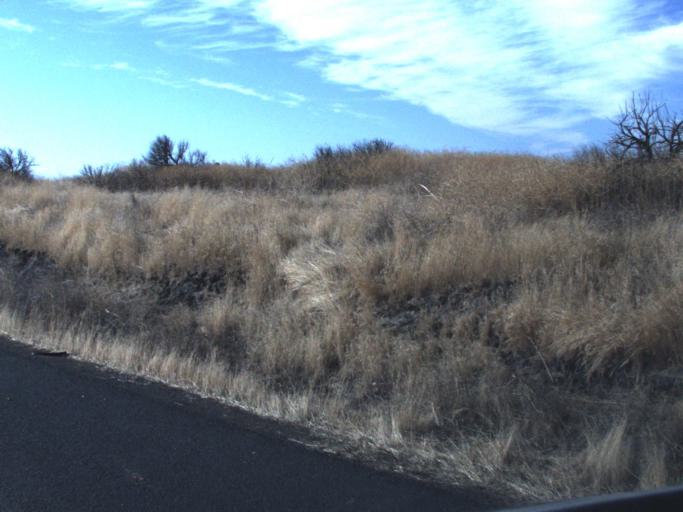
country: US
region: Washington
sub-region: Franklin County
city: Connell
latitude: 46.6545
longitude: -119.0064
